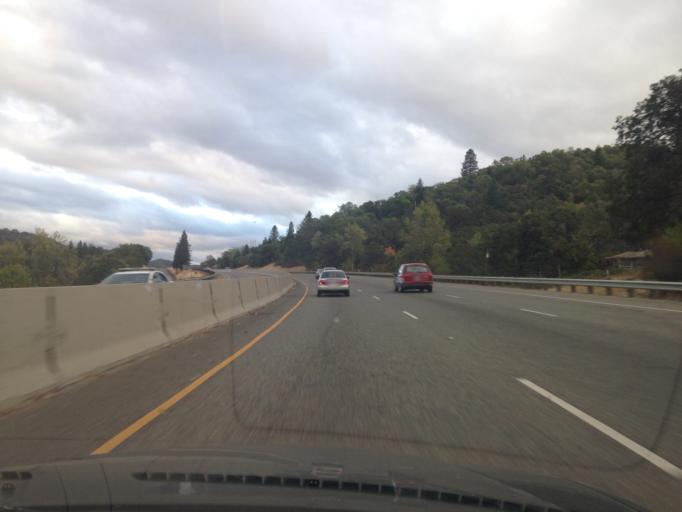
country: US
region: Oregon
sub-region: Douglas County
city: Green
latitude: 43.1822
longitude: -123.3741
